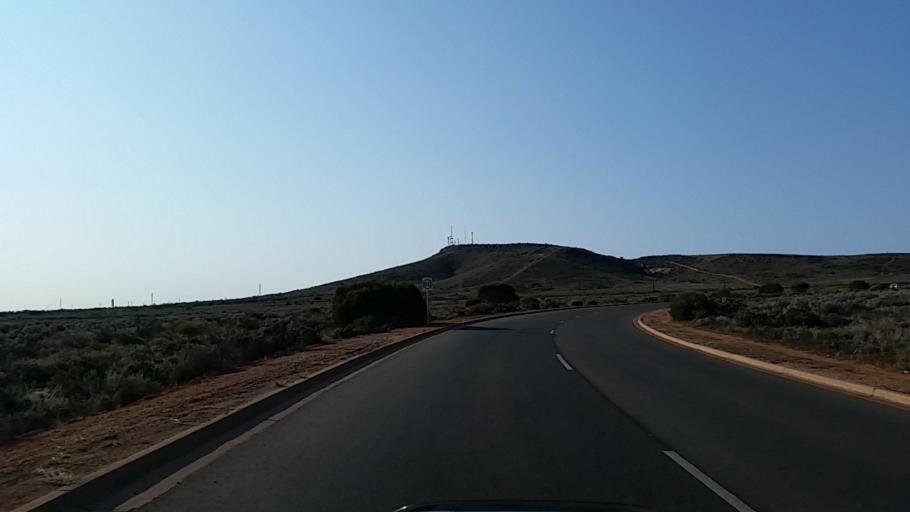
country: AU
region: South Australia
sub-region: Whyalla
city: Whyalla
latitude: -33.0112
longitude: 137.5280
